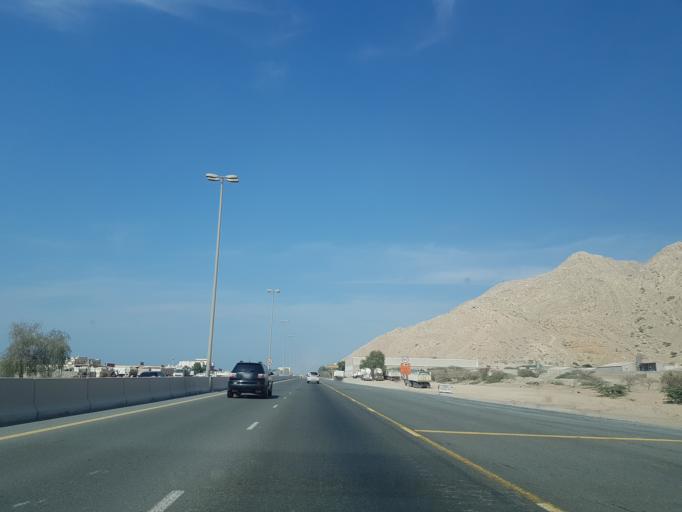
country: AE
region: Ra's al Khaymah
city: Ras al-Khaimah
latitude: 25.8525
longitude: 56.0203
